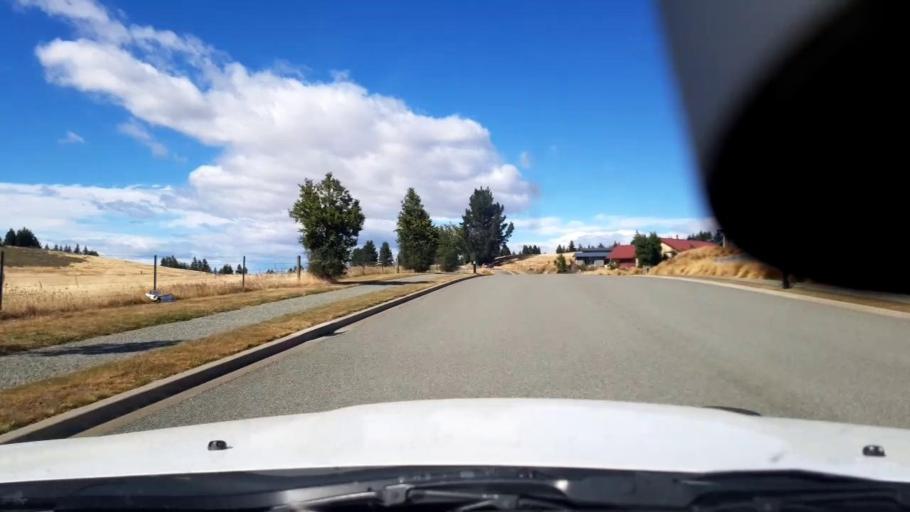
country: NZ
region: Canterbury
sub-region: Timaru District
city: Pleasant Point
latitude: -44.0076
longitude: 170.4744
